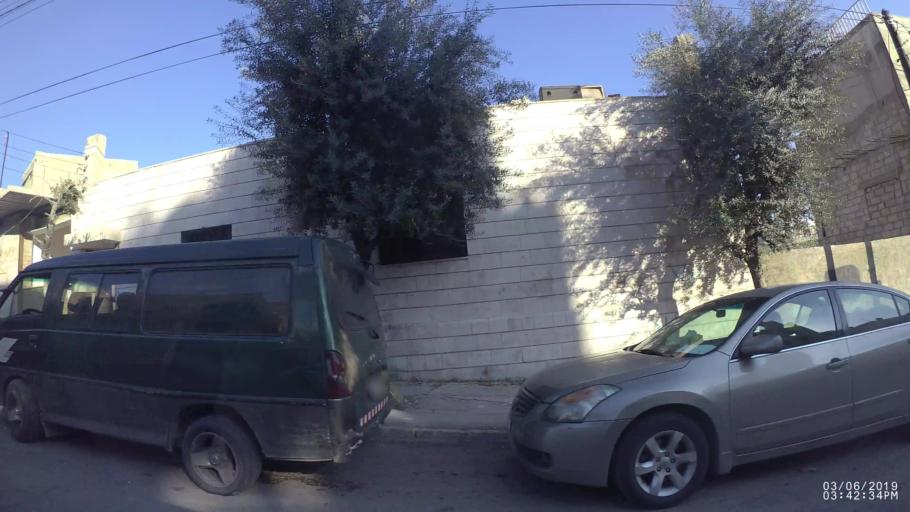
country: JO
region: Amman
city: Amman
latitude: 31.9653
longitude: 35.9596
